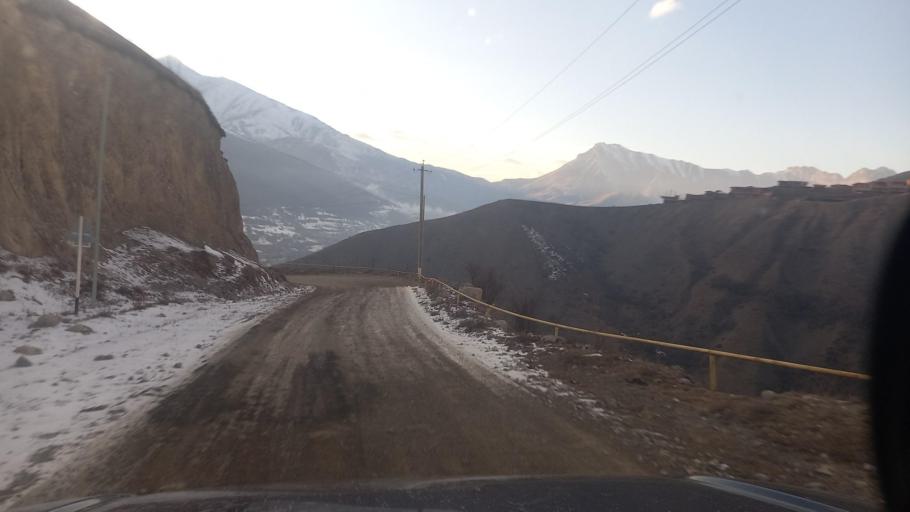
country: RU
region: Ingushetiya
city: Dzhayrakh
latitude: 42.8251
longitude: 44.7081
